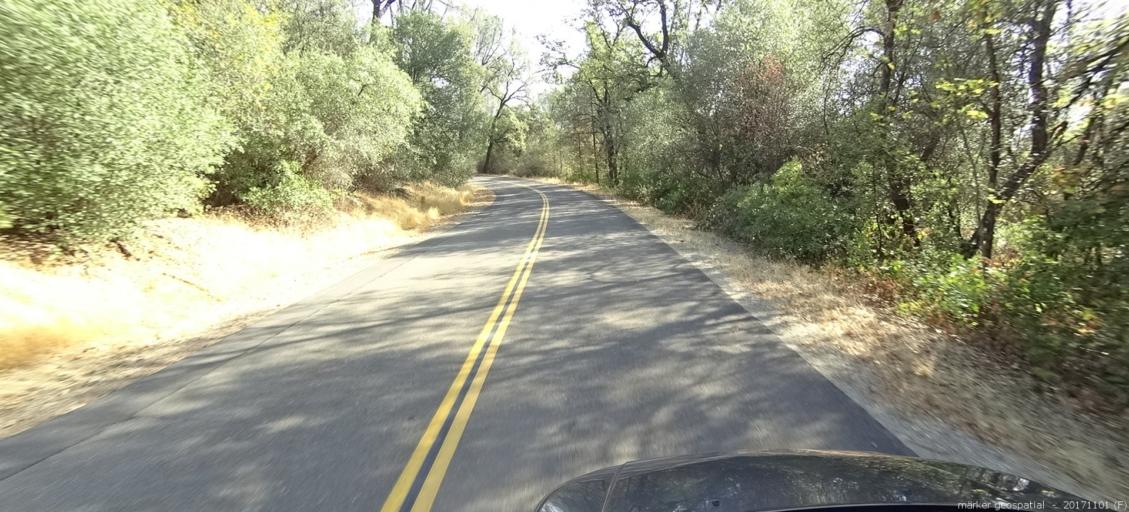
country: US
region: California
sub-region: Shasta County
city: Central Valley (historical)
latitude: 40.6753
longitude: -122.4051
